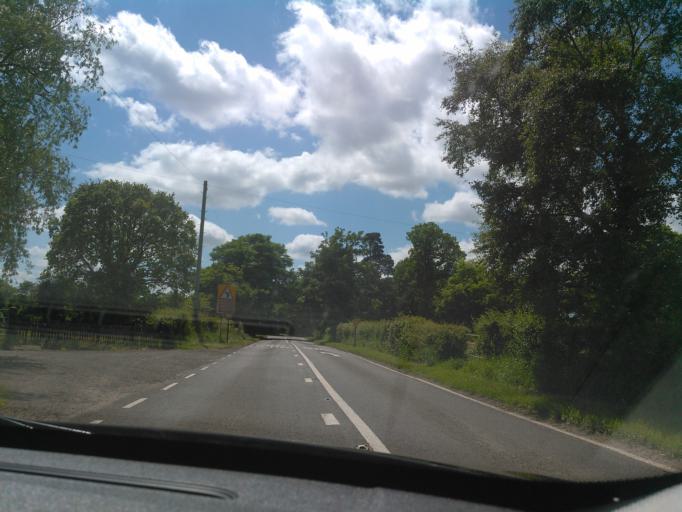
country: GB
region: England
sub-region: Shropshire
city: Prees
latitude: 52.8929
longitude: -2.6304
